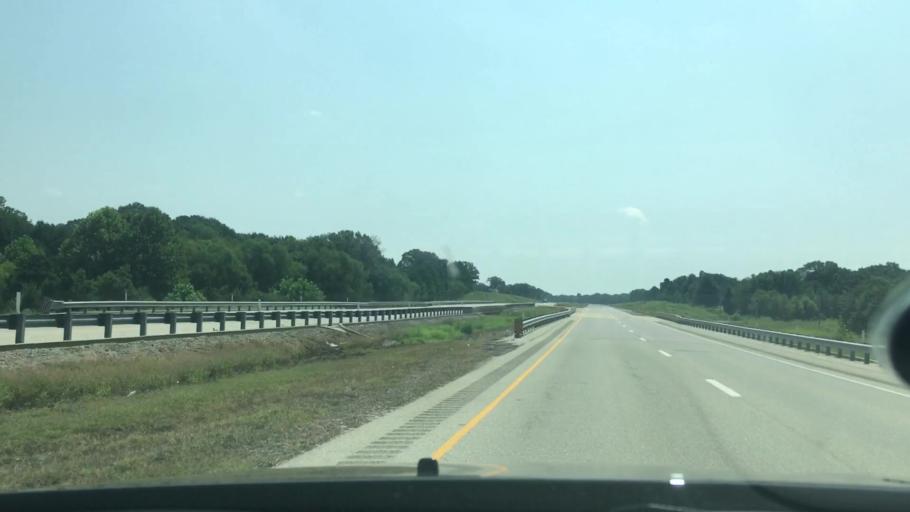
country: US
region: Oklahoma
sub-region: Atoka County
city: Atoka
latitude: 34.3246
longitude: -96.0423
